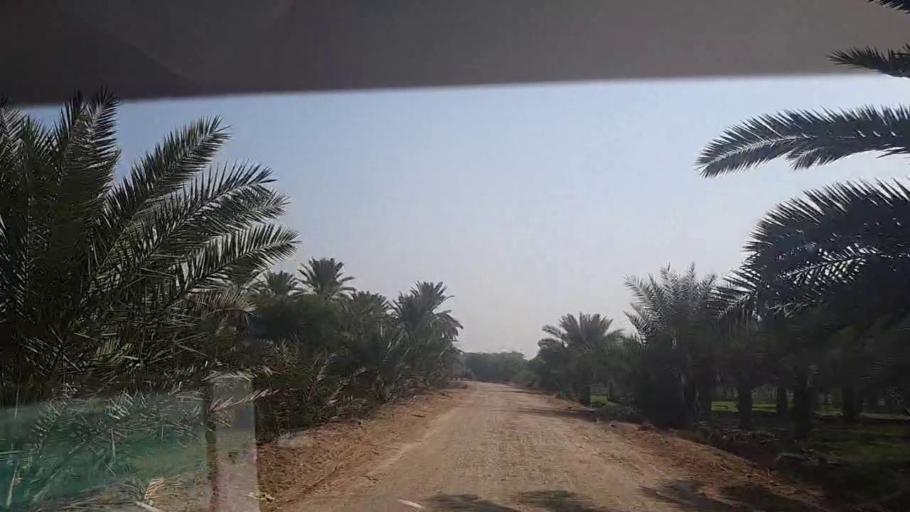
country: PK
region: Sindh
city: Kot Diji
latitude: 27.4338
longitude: 68.6878
